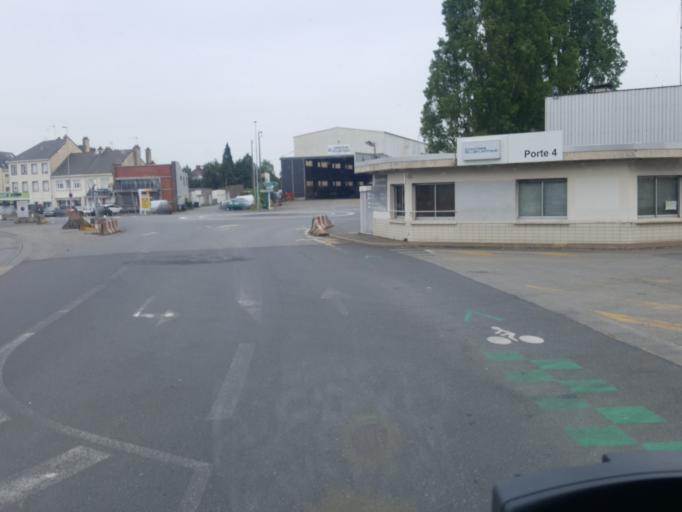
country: FR
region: Pays de la Loire
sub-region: Departement de la Loire-Atlantique
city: Saint-Nazaire
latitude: 47.2891
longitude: -2.1922
